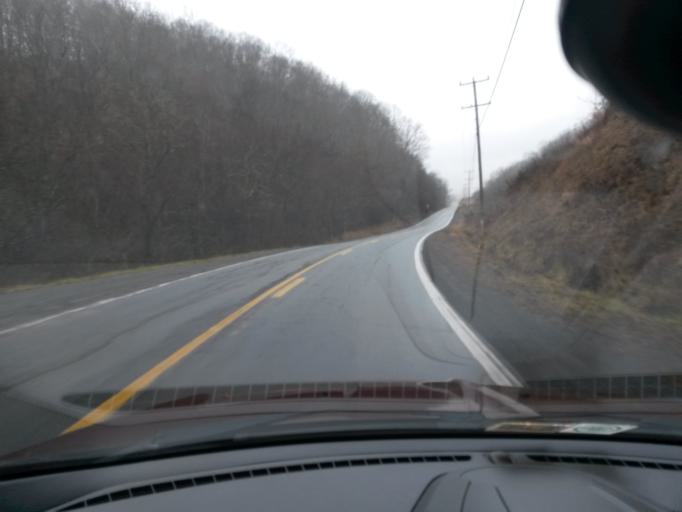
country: US
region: West Virginia
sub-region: Greenbrier County
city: Lewisburg
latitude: 37.8716
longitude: -80.5127
